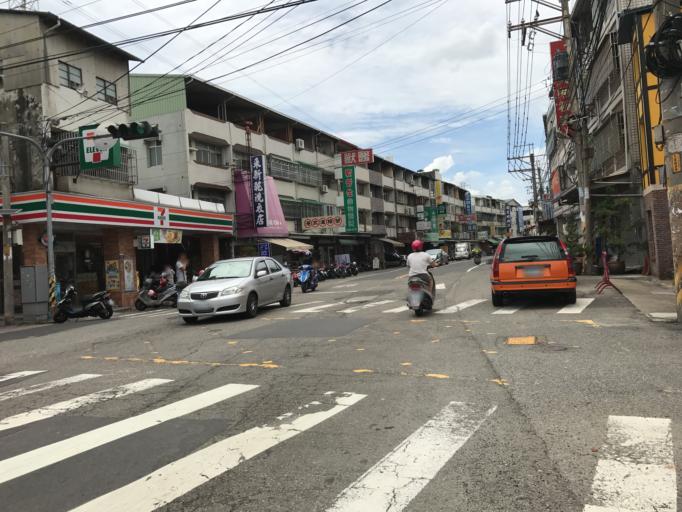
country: TW
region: Taiwan
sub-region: Taichung City
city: Taichung
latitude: 24.0853
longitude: 120.7085
